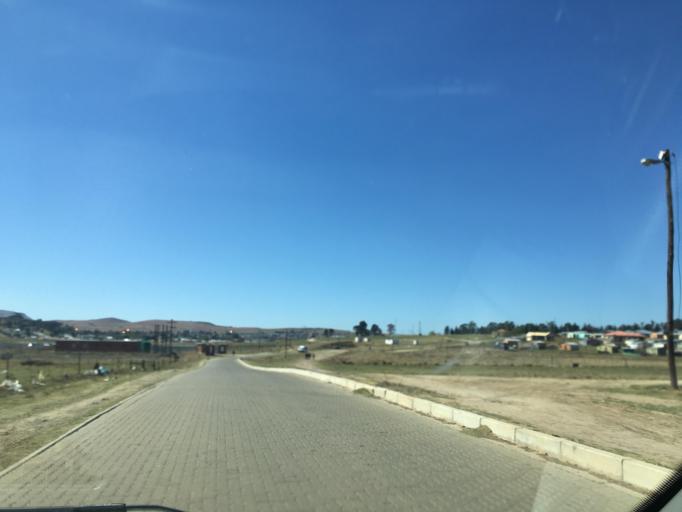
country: ZA
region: Eastern Cape
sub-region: Chris Hani District Municipality
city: Elliot
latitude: -31.3312
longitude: 27.8303
